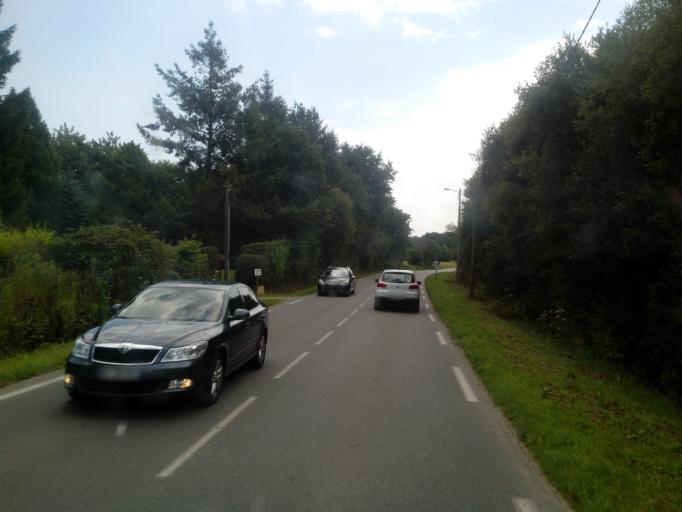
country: FR
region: Brittany
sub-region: Departement des Cotes-d'Armor
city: Plouha
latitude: 48.6926
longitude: -2.9356
